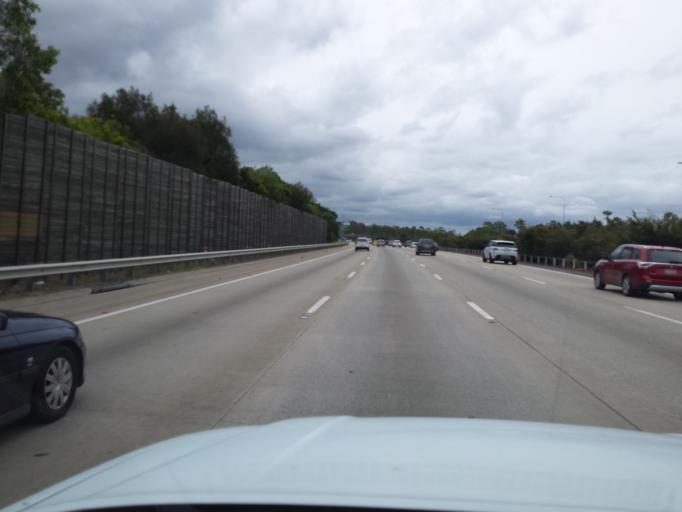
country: AU
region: Queensland
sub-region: Gold Coast
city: Upper Coomera
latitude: -27.9332
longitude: 153.3344
